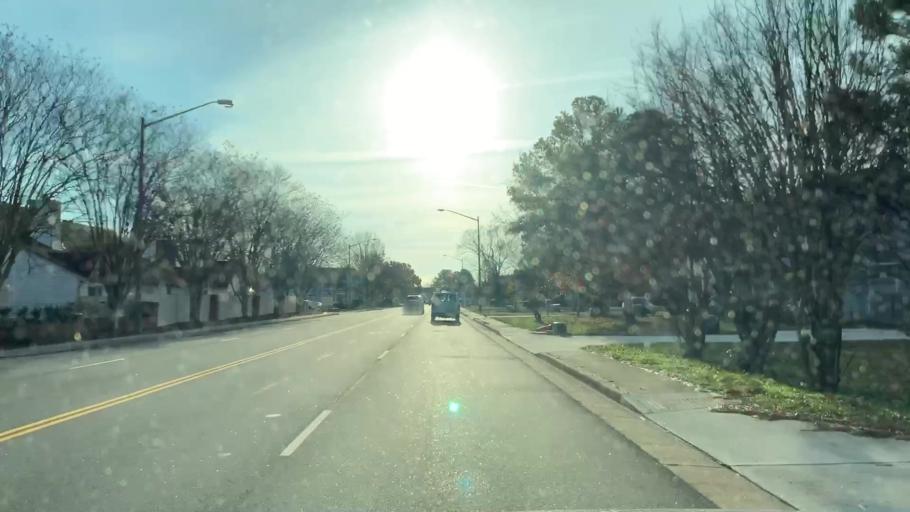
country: US
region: Virginia
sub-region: City of Chesapeake
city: Chesapeake
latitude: 36.7913
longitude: -76.1668
